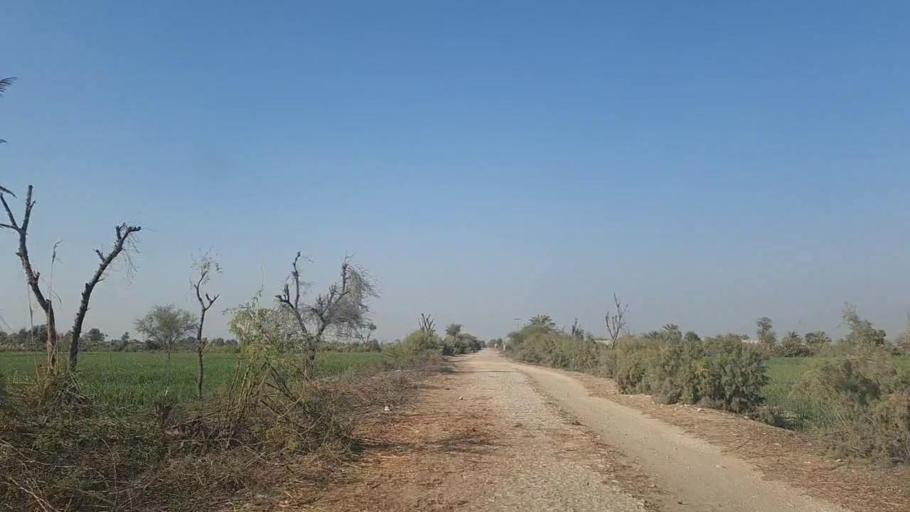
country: PK
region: Sindh
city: Jam Sahib
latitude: 26.3172
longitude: 68.7148
